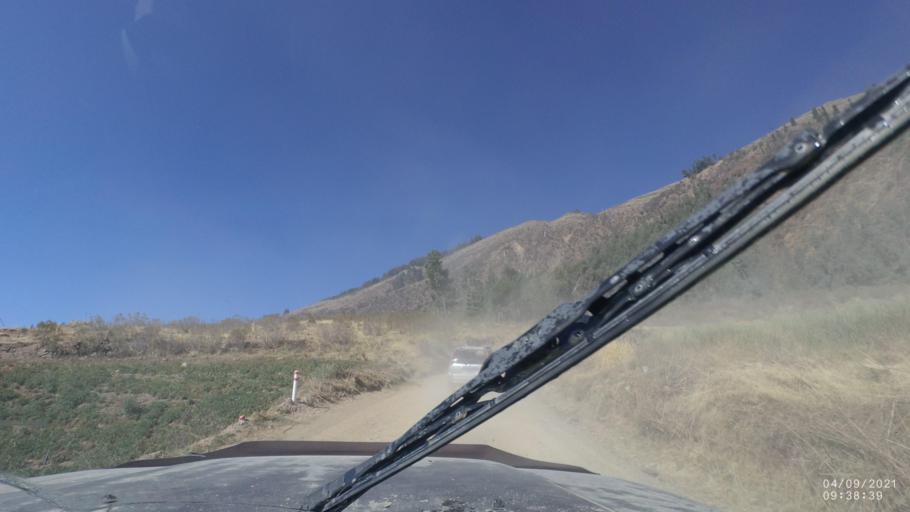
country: BO
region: Cochabamba
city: Sipe Sipe
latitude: -17.3463
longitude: -66.3838
